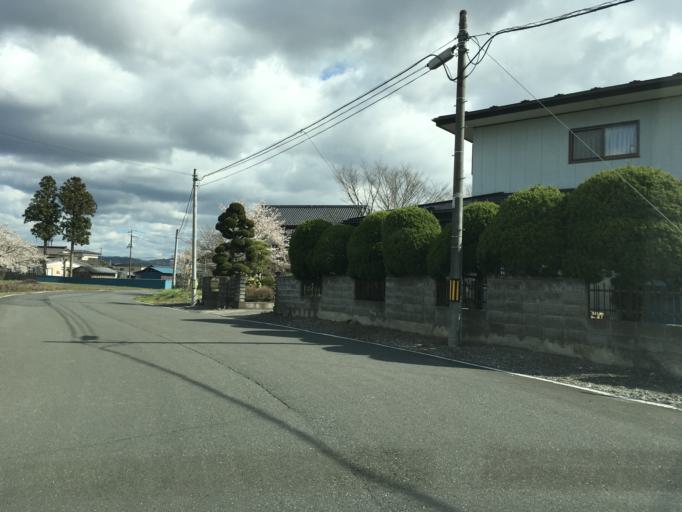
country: JP
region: Iwate
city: Ichinoseki
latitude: 38.7435
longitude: 141.2640
